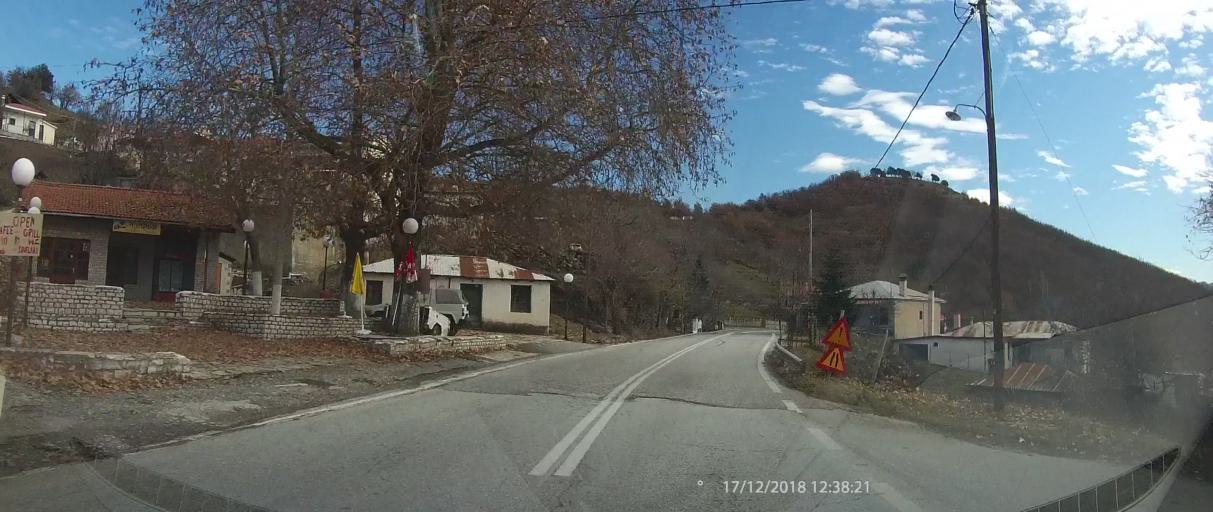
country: GR
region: Epirus
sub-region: Nomos Ioanninon
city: Metsovo
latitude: 39.8096
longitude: 21.3457
